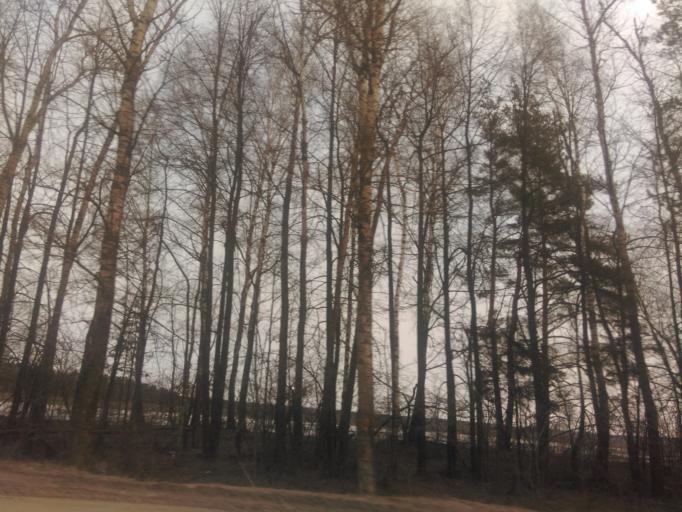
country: RU
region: Moskovskaya
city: Tuchkovo
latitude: 55.5643
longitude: 36.5328
